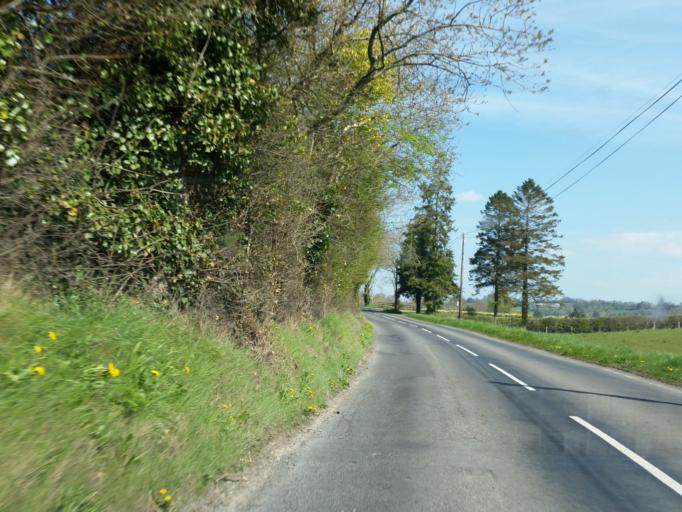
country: GB
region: Northern Ireland
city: Lisnaskea
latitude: 54.3010
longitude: -7.4166
